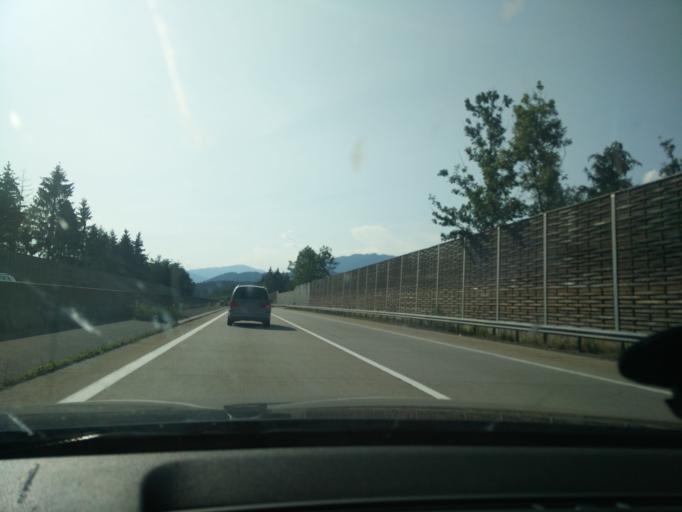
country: AT
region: Carinthia
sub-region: Politischer Bezirk Villach Land
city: Wernberg
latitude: 46.6210
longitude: 13.9788
